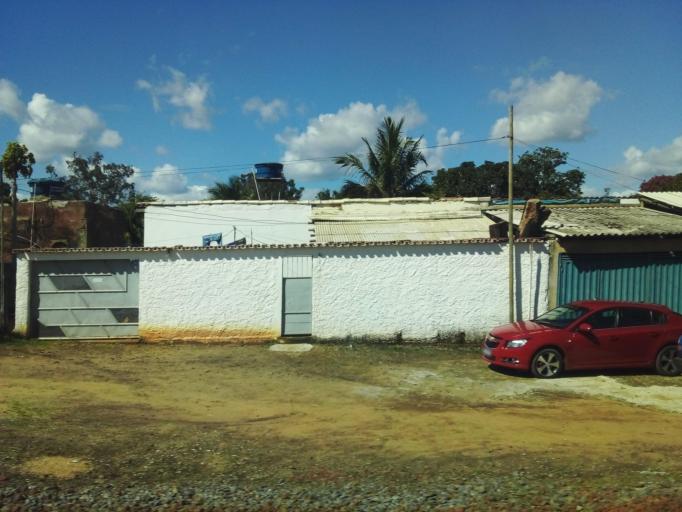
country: BR
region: Minas Gerais
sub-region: Governador Valadares
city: Governador Valadares
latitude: -18.8405
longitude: -41.8756
